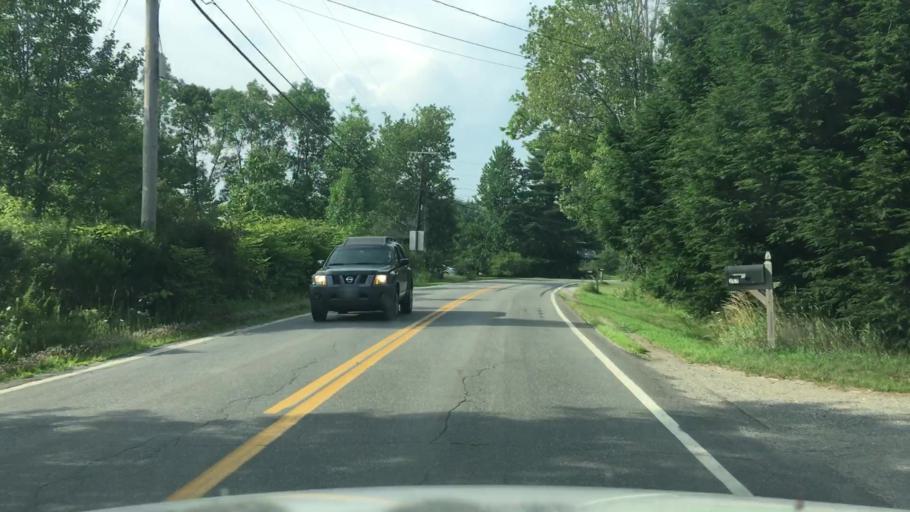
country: US
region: Maine
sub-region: Lincoln County
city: Waldoboro
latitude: 44.1126
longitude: -69.3660
